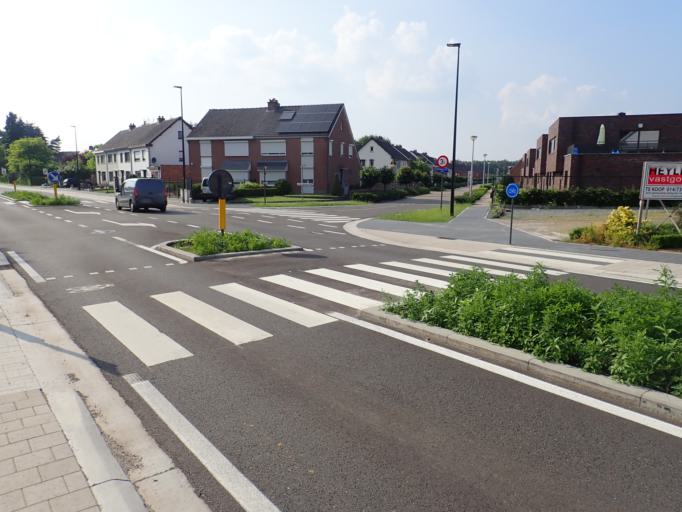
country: BE
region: Flanders
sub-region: Provincie Antwerpen
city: Kasterlee
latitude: 51.2244
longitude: 4.9050
